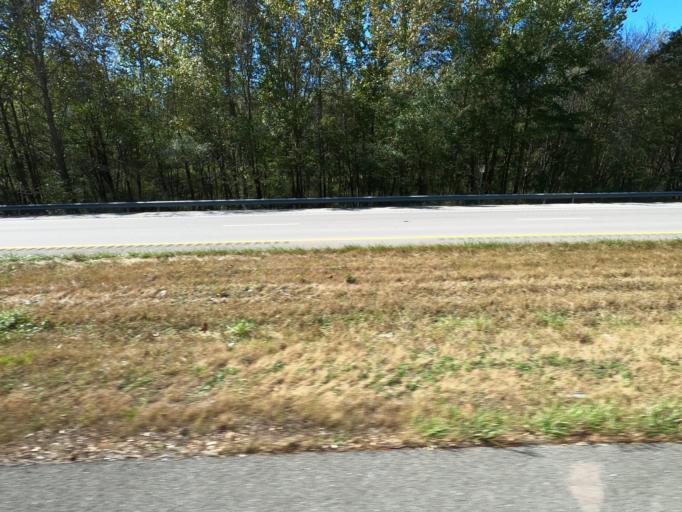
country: US
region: Tennessee
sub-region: Maury County
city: Mount Pleasant
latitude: 35.4050
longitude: -87.2806
